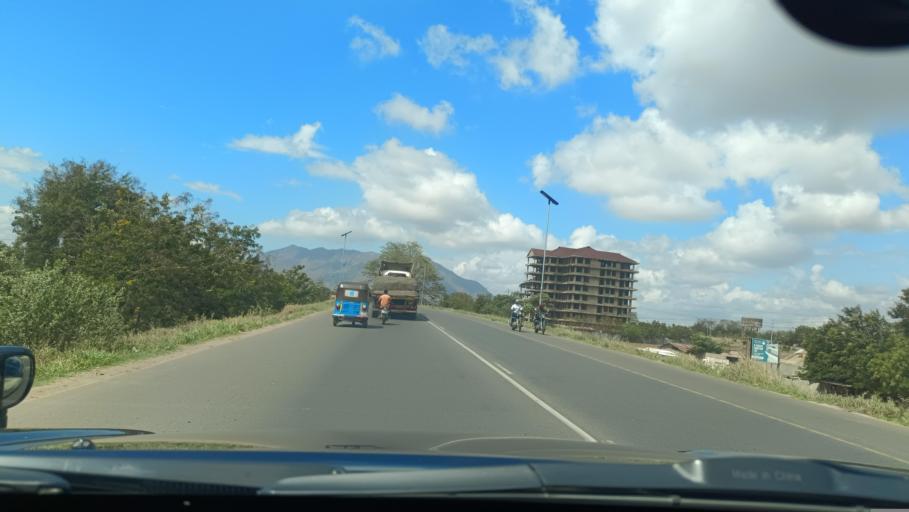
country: TZ
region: Morogoro
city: Morogoro
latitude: -6.8060
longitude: 37.6580
